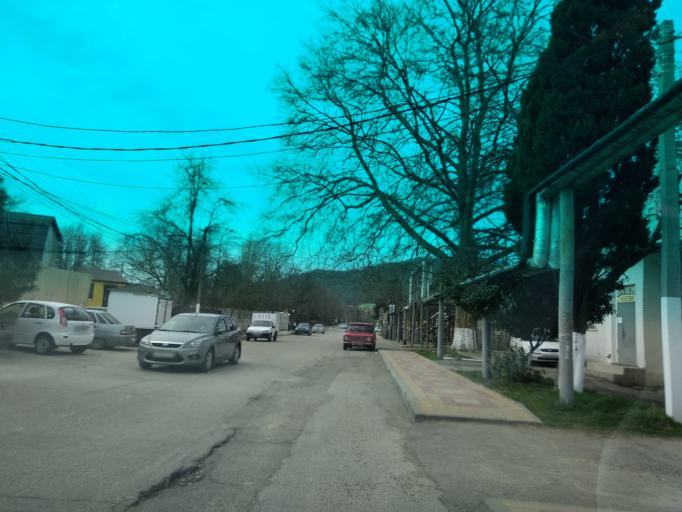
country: RU
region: Krasnodarskiy
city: Novomikhaylovskiy
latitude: 44.2498
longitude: 38.8408
